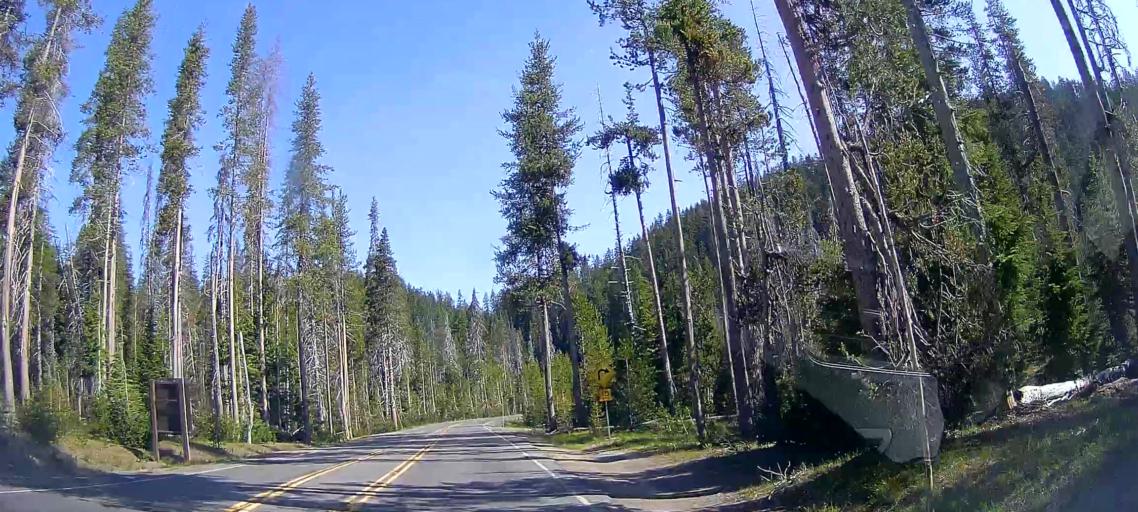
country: US
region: Oregon
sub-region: Jackson County
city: Shady Cove
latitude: 42.8701
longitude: -122.1697
